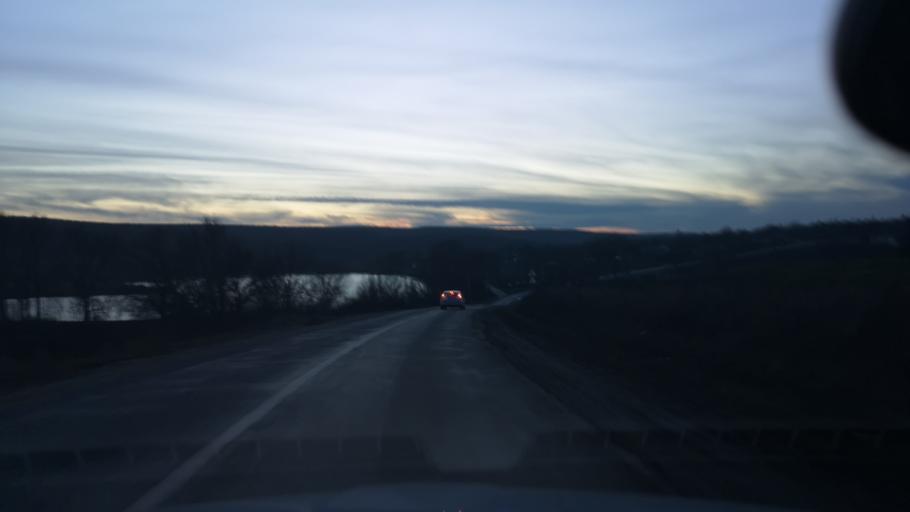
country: MD
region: Orhei
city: Orhei
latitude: 47.2866
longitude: 28.8778
